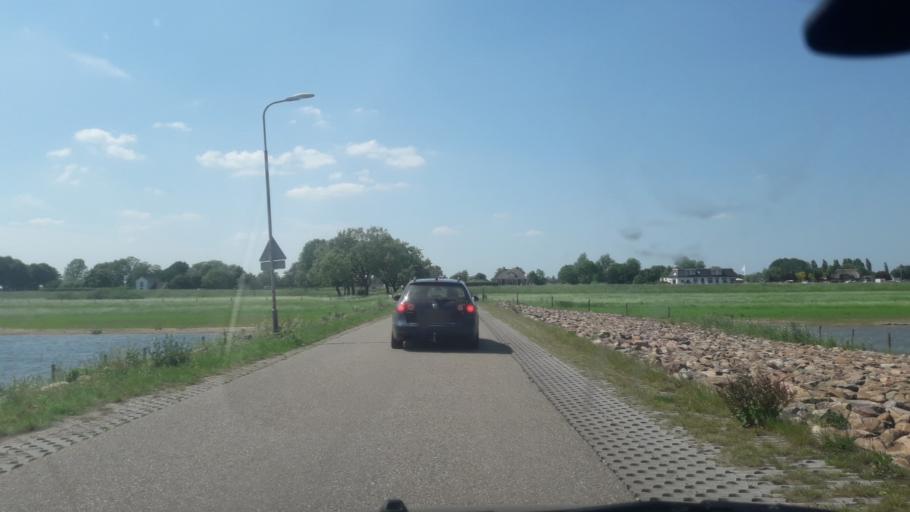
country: NL
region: Overijssel
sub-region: Gemeente Olst-Wijhe
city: Olst
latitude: 52.3416
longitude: 6.1005
